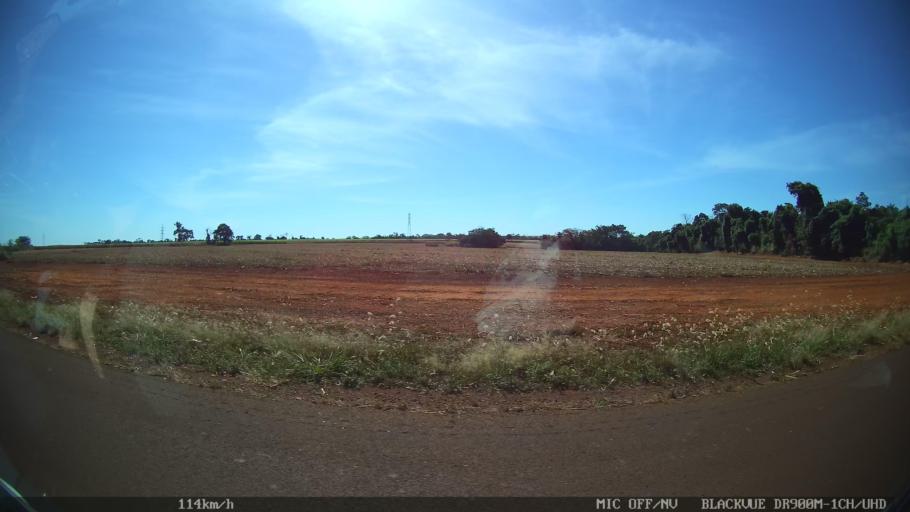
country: BR
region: Sao Paulo
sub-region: Guaira
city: Guaira
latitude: -20.4434
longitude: -48.3343
